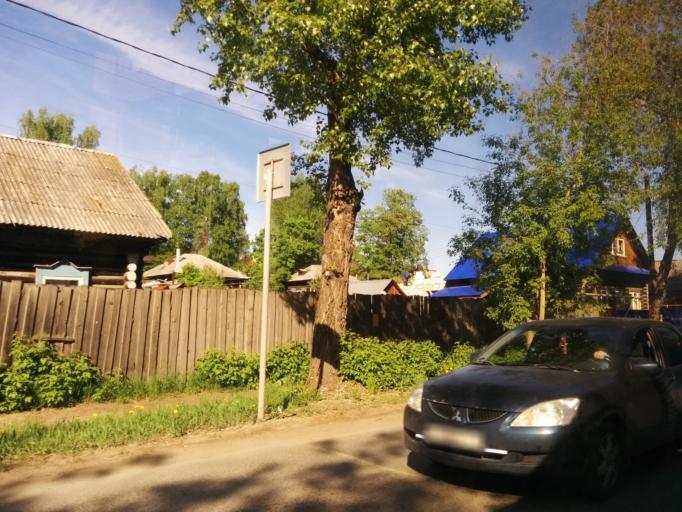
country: RU
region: Perm
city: Kondratovo
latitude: 58.0441
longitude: 56.1009
